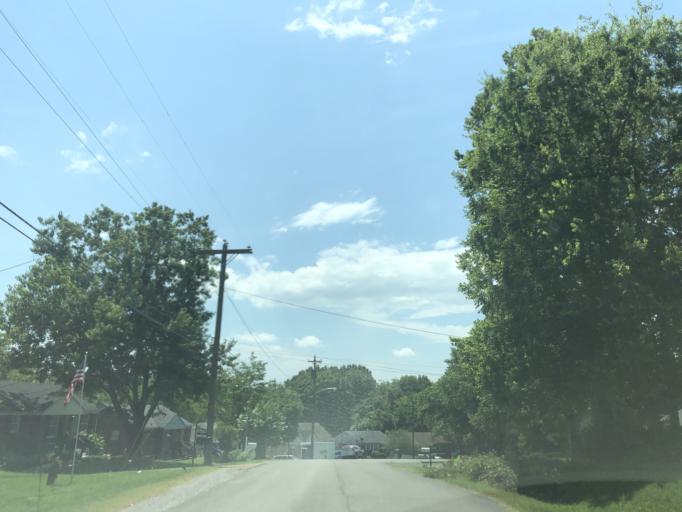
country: US
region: Tennessee
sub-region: Davidson County
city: Lakewood
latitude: 36.1557
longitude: -86.6545
